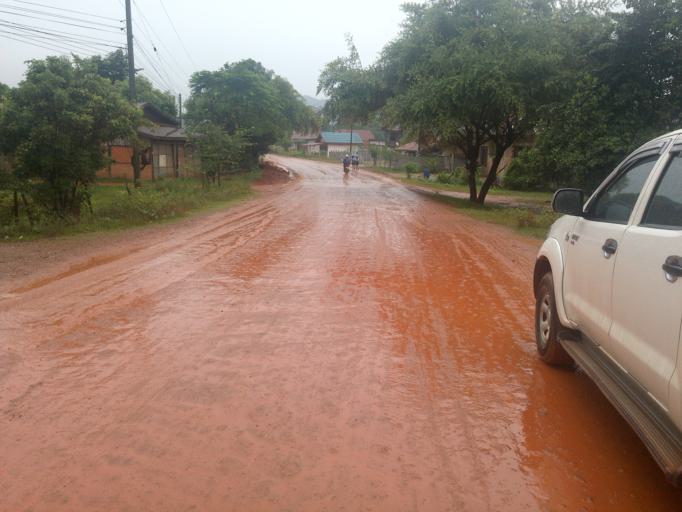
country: LA
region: Bolikhamxai
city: Bolikhan
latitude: 18.5563
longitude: 103.7259
